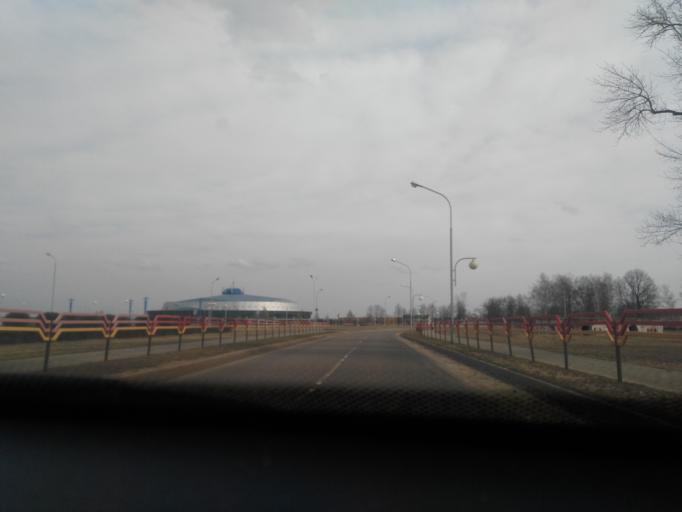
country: BY
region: Mogilev
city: Babruysk
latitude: 53.1430
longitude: 29.2405
